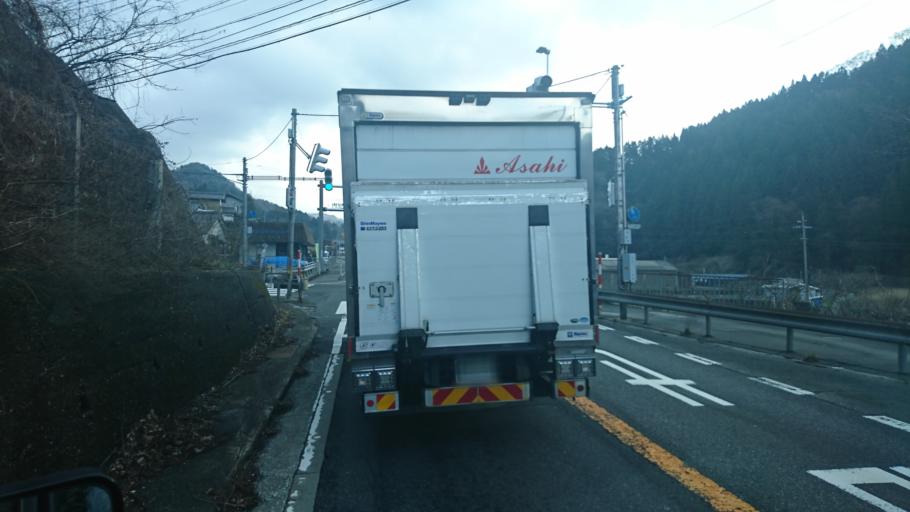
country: JP
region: Tottori
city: Tottori
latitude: 35.5497
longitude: 134.4961
